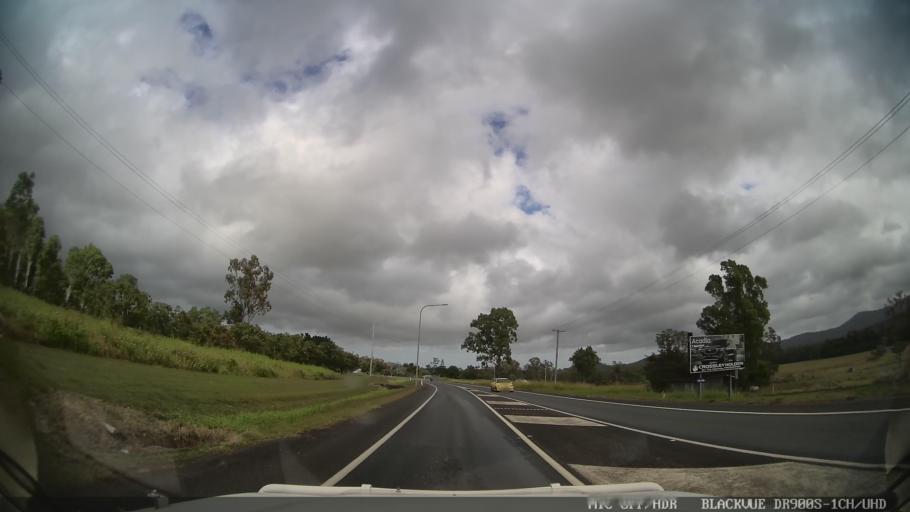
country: AU
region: Queensland
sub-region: Whitsunday
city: Proserpine
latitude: -20.3098
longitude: 148.6584
